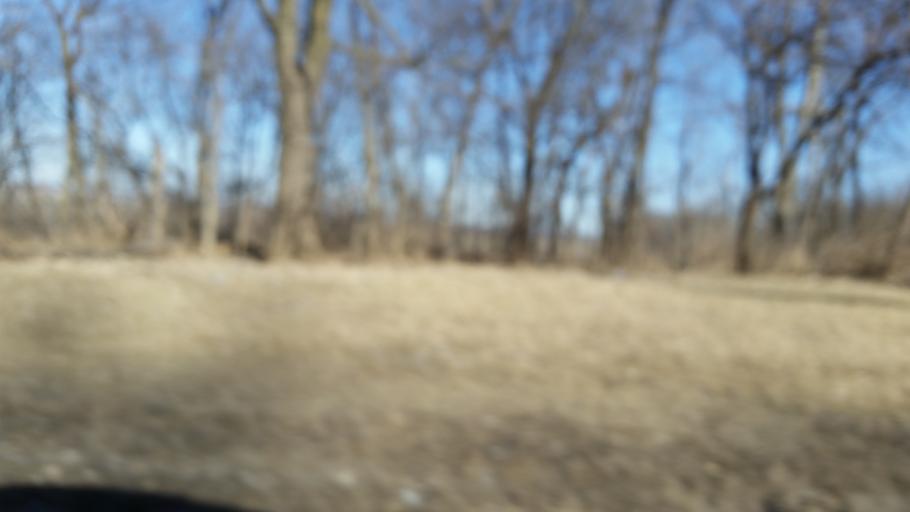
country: US
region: Nebraska
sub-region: Douglas County
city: Omaha
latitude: 41.1971
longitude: -95.9335
